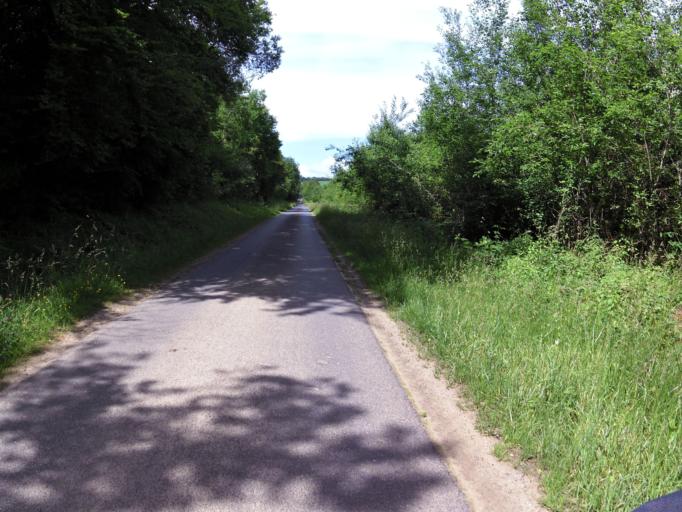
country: FR
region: Champagne-Ardenne
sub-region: Departement des Ardennes
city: Mouzon
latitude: 49.5384
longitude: 5.0864
